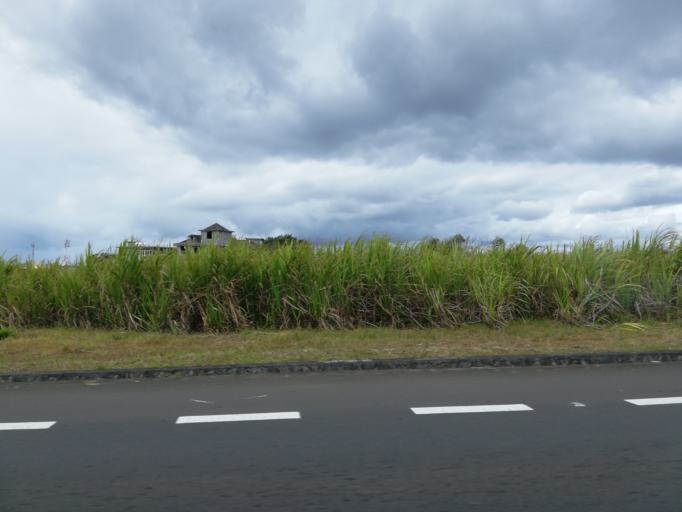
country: MU
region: Moka
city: Quartier Militaire
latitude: -20.2420
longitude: 57.5966
